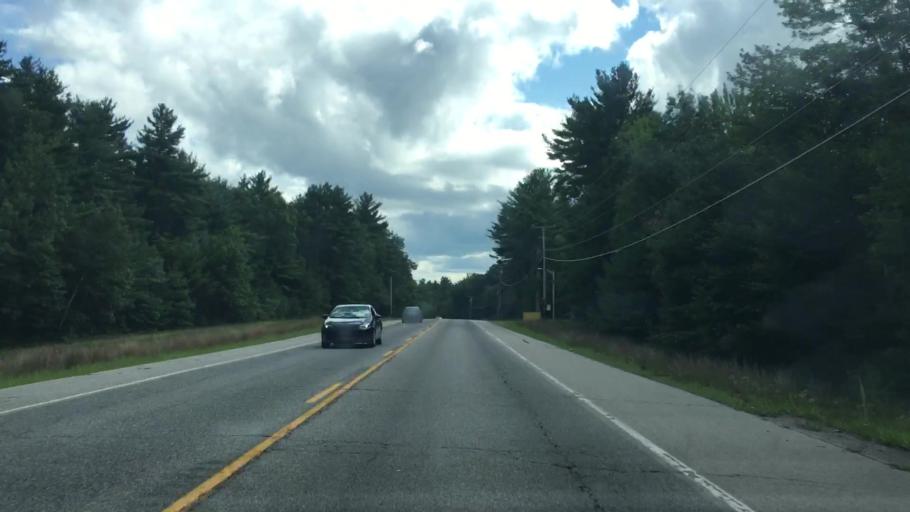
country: US
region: Maine
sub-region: York County
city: South Sanford
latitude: 43.3816
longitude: -70.7405
